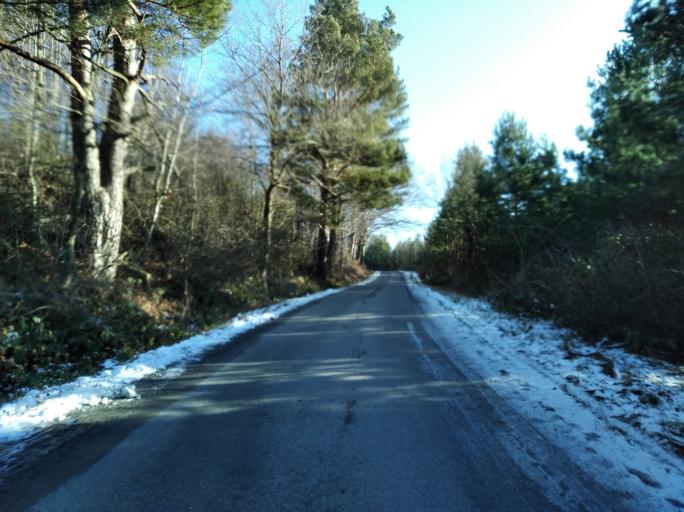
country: PL
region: Subcarpathian Voivodeship
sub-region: Powiat strzyzowski
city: Konieczkowa
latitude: 49.8601
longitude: 21.9520
